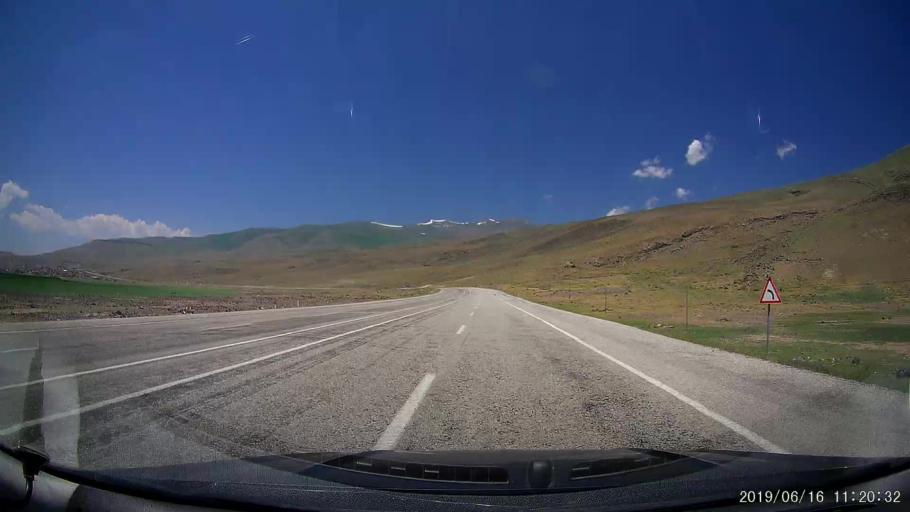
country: TR
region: Agri
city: Dogubayazit
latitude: 39.6994
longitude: 44.0882
